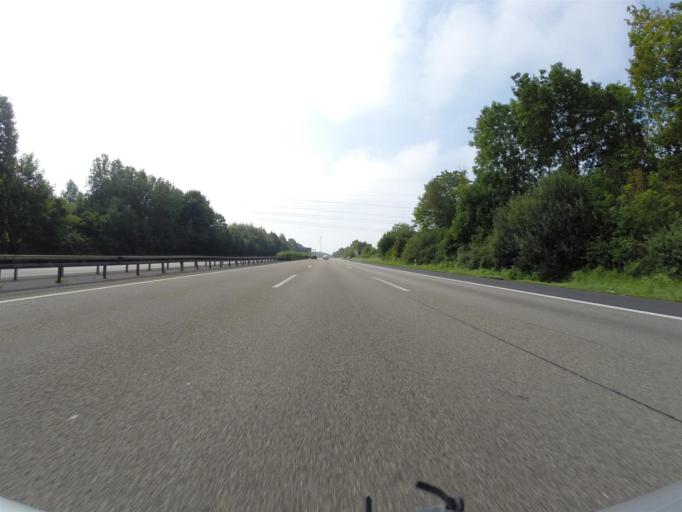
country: DE
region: Hesse
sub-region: Regierungsbezirk Kassel
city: Lohfelden
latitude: 51.2603
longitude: 9.5167
